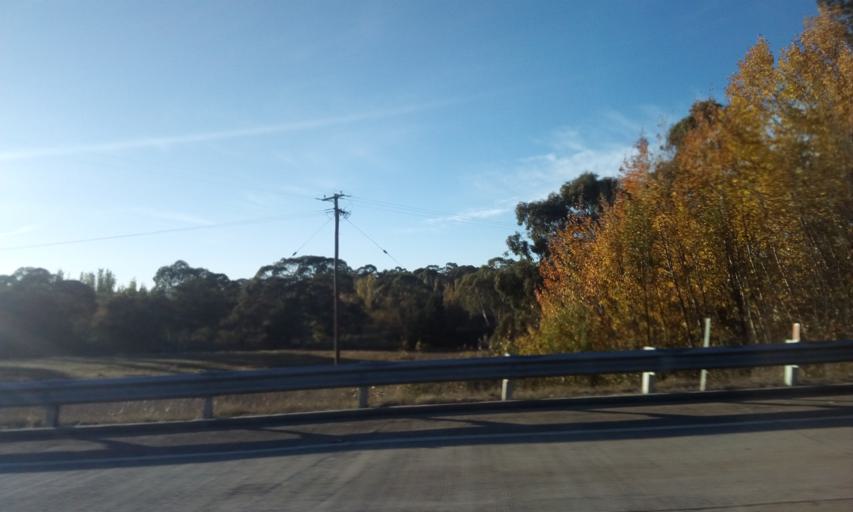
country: AU
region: New South Wales
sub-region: Yass Valley
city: Gundaroo
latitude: -35.1441
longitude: 149.3339
